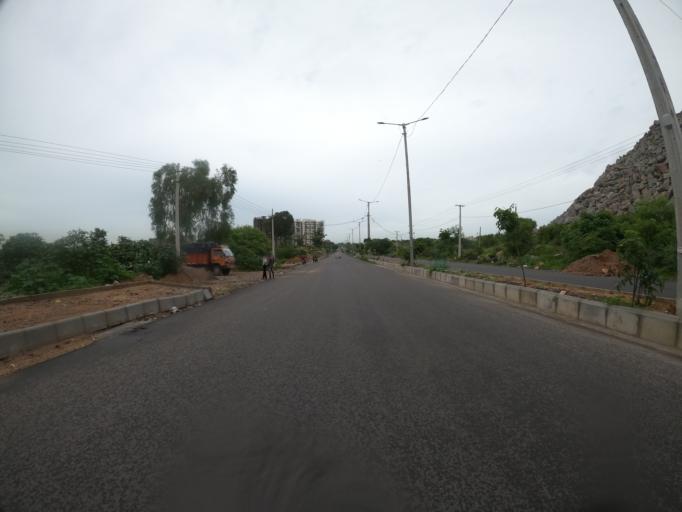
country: IN
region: Telangana
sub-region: Rangareddi
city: Kukatpalli
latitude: 17.4626
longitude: 78.3875
